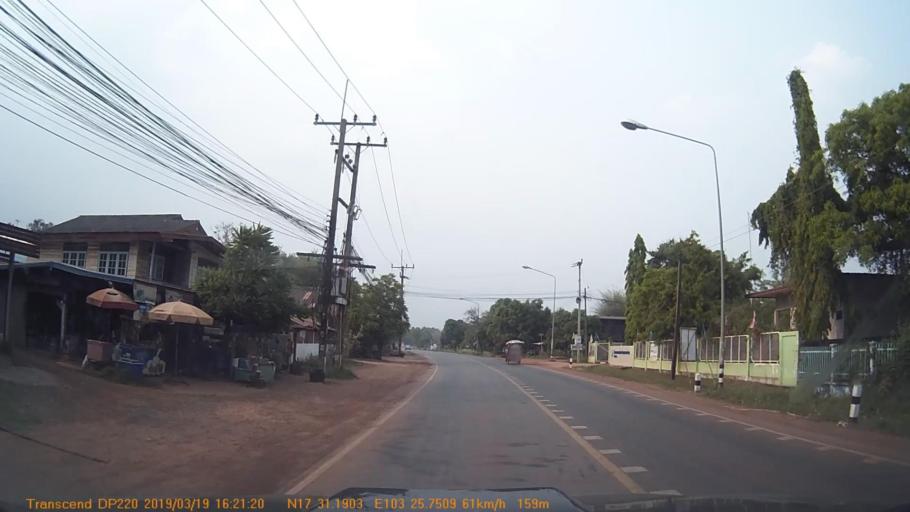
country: TH
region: Sakon Nakhon
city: Sawang Daen Din
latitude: 17.5204
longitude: 103.4291
